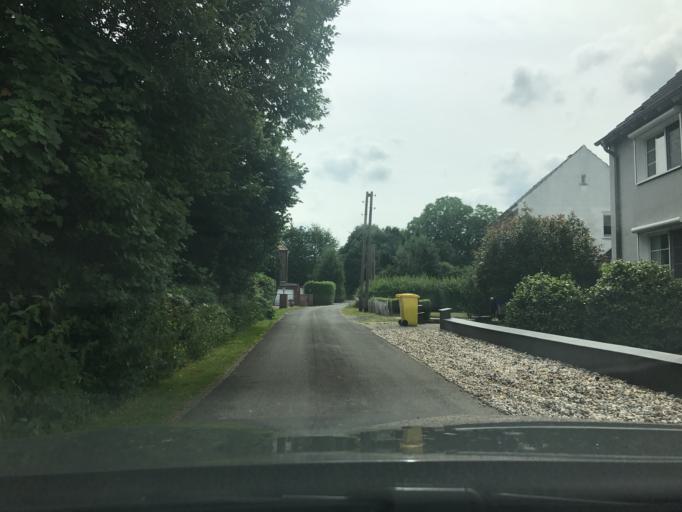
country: DE
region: North Rhine-Westphalia
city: Kempen
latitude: 51.3365
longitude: 6.4142
